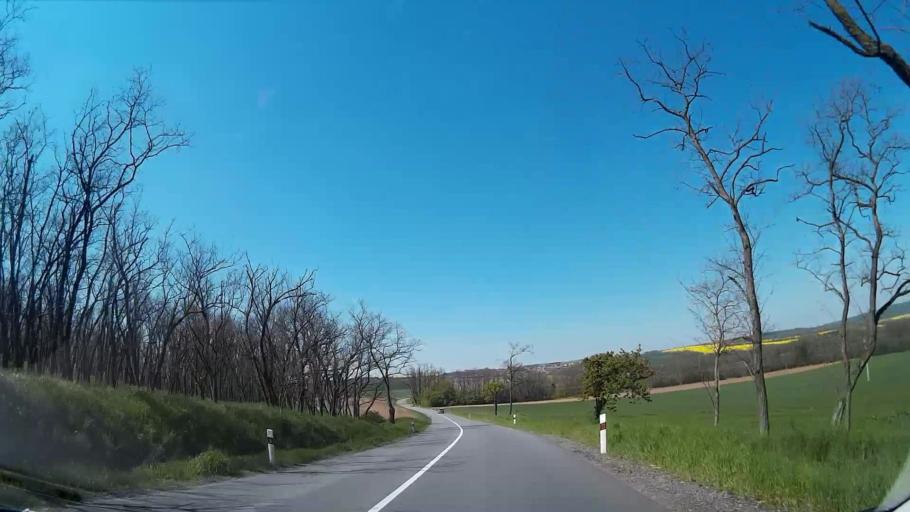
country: CZ
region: South Moravian
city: Moravsky Krumlov
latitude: 49.0769
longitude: 16.3330
